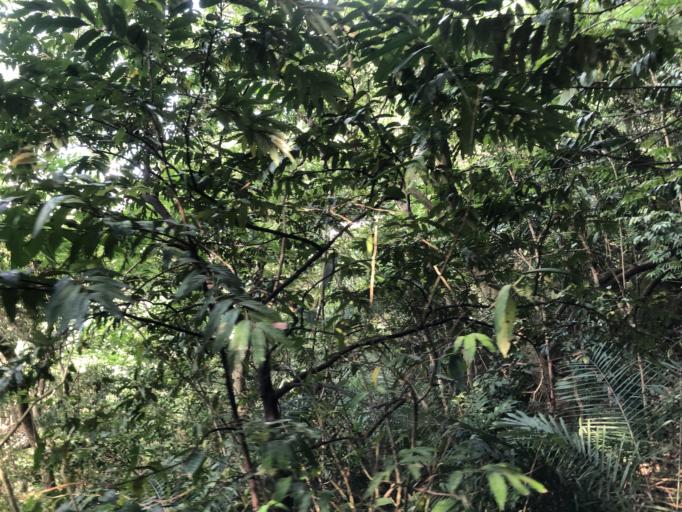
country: TW
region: Taipei
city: Taipei
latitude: 25.1039
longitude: 121.5307
